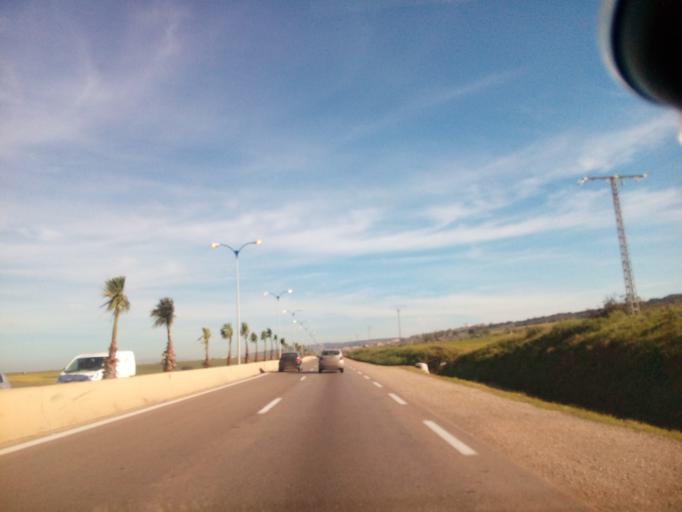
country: DZ
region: Mostaganem
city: Mostaganem
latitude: 35.8153
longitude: -0.0271
